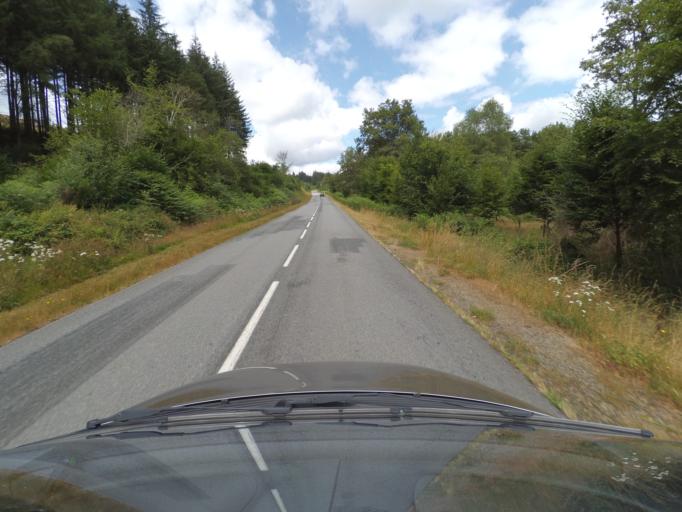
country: FR
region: Limousin
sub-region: Departement de la Creuse
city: Bourganeuf
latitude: 45.9182
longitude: 1.8474
